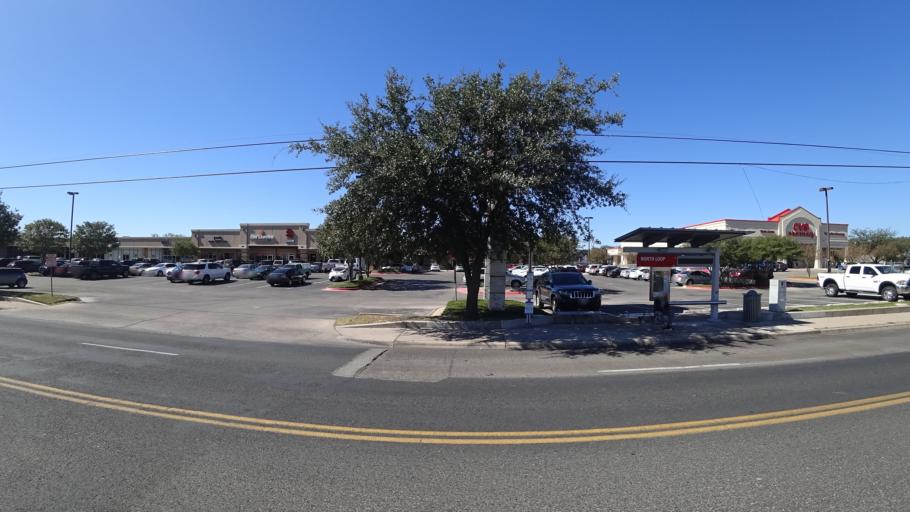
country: US
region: Texas
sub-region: Travis County
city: Austin
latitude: 30.3249
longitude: -97.7396
